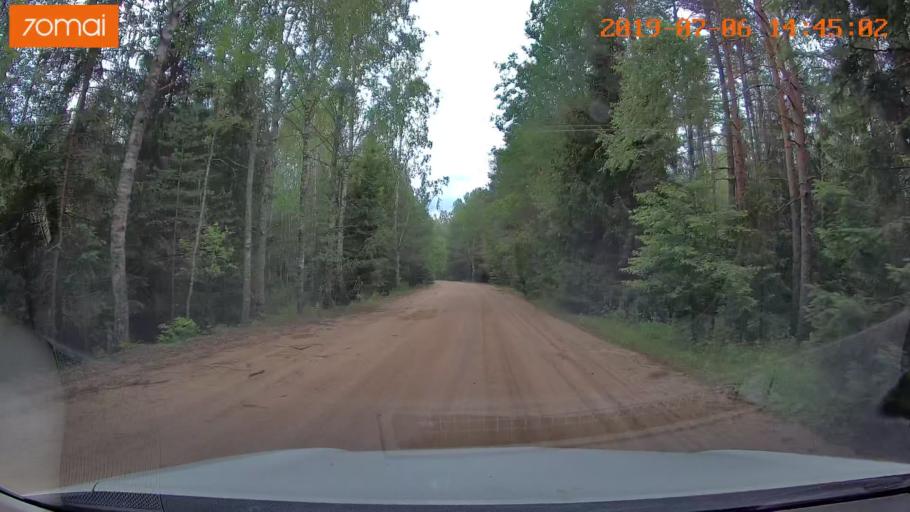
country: BY
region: Minsk
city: Ivyanyets
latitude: 53.9682
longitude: 26.6896
